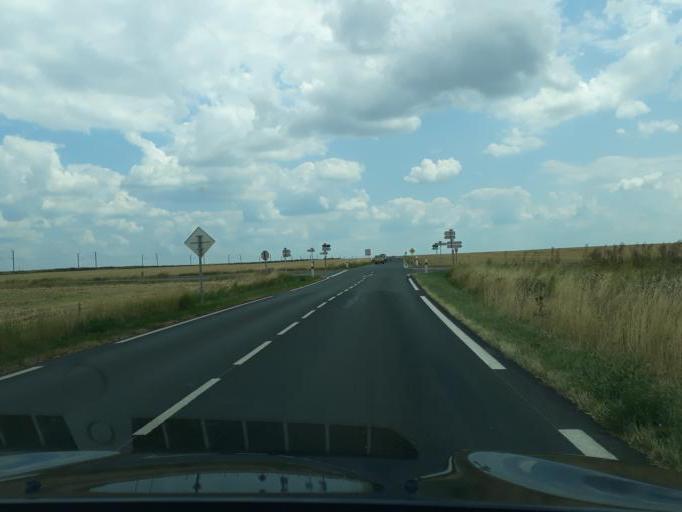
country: FR
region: Centre
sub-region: Departement du Cher
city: Avord
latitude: 47.0165
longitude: 2.7102
